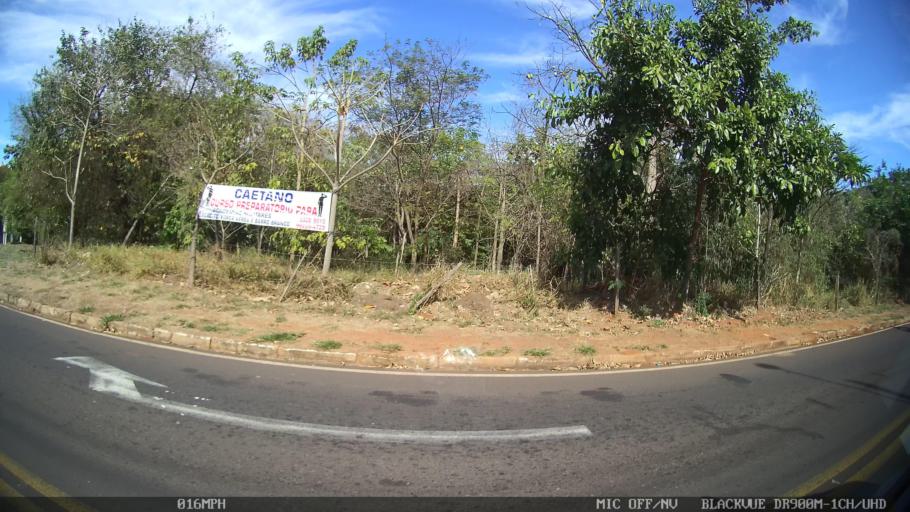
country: BR
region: Sao Paulo
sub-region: Sao Jose Do Rio Preto
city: Sao Jose do Rio Preto
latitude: -20.8418
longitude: -49.3533
